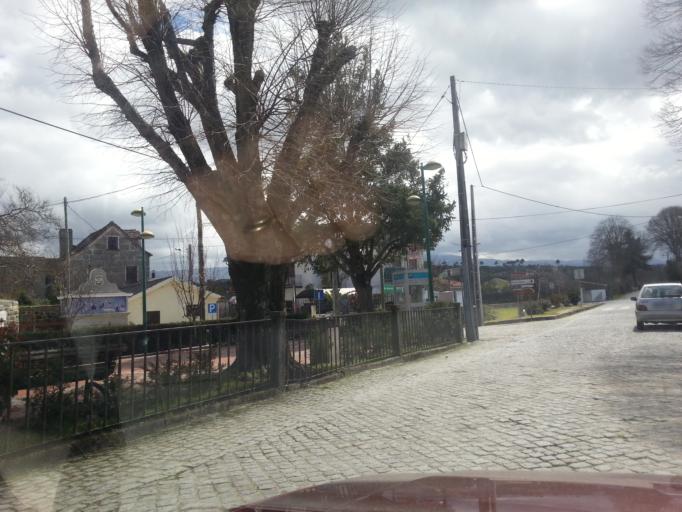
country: PT
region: Guarda
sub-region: Fornos de Algodres
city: Fornos de Algodres
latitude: 40.5872
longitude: -7.5395
